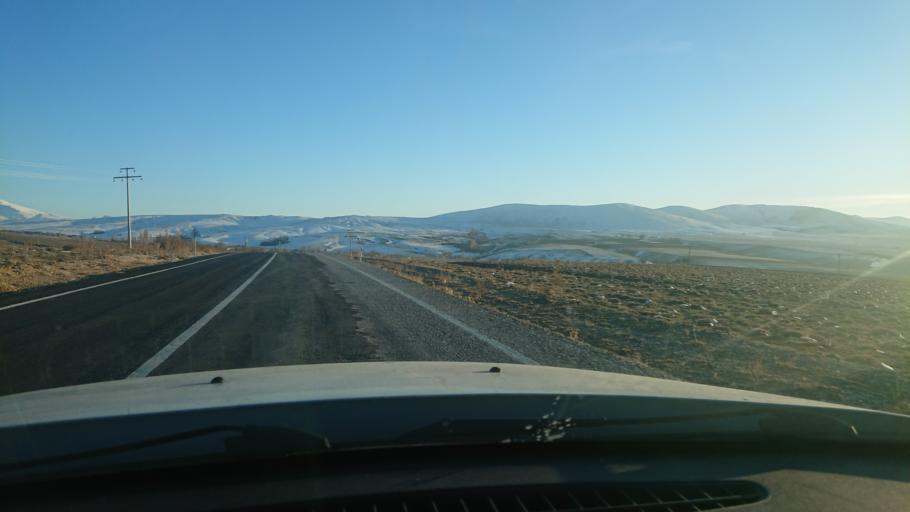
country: TR
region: Aksaray
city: Ortakoy
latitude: 38.7642
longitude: 33.9318
